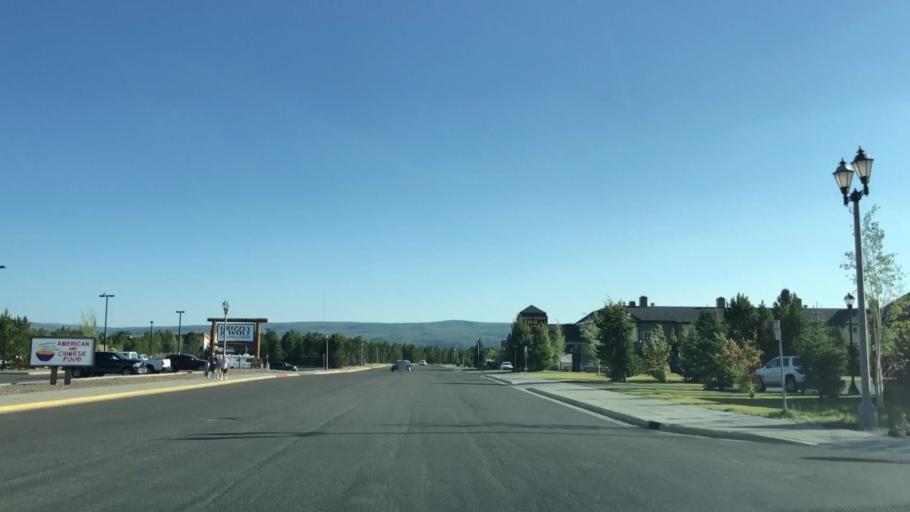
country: US
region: Montana
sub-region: Gallatin County
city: West Yellowstone
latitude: 44.6572
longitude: -111.0997
